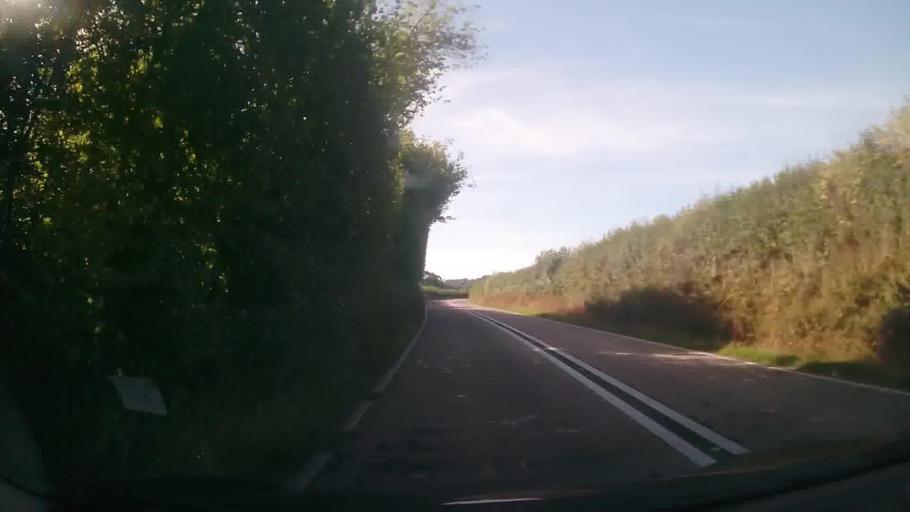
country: GB
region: Wales
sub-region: Sir Powys
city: Hay
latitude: 51.9786
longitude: -3.2231
